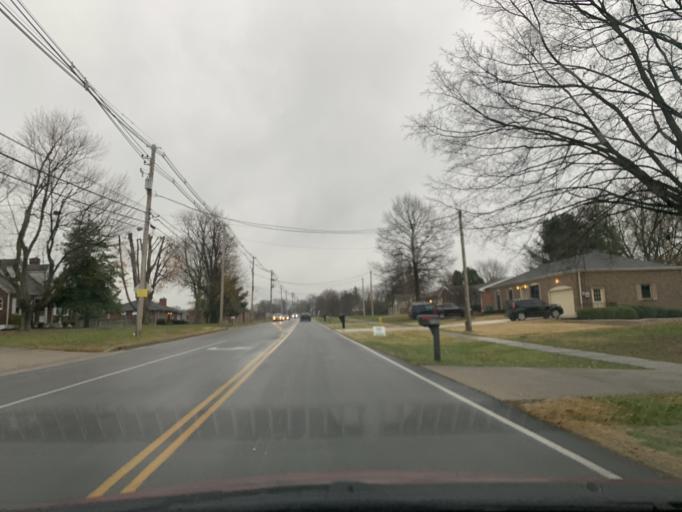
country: US
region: Kentucky
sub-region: Jefferson County
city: Saint Regis Park
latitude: 38.2005
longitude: -85.6145
